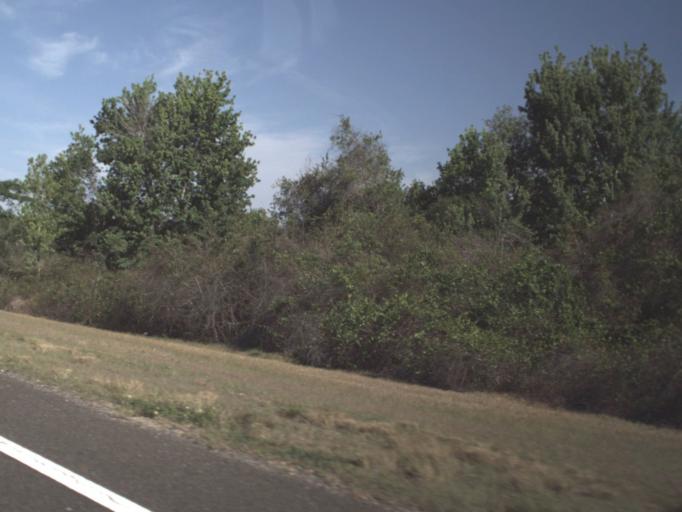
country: US
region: Florida
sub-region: Lake County
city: Minneola
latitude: 28.6388
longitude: -81.7870
